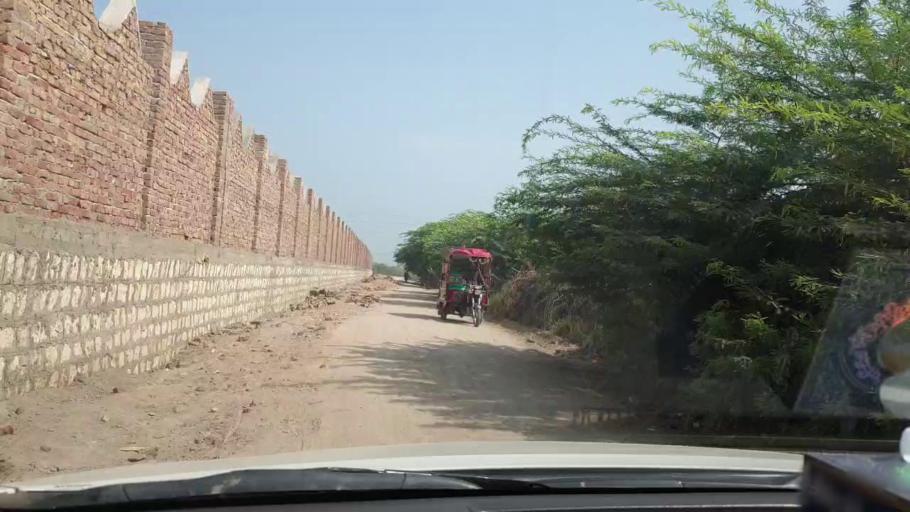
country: PK
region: Sindh
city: Shikarpur
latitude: 27.9694
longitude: 68.6658
